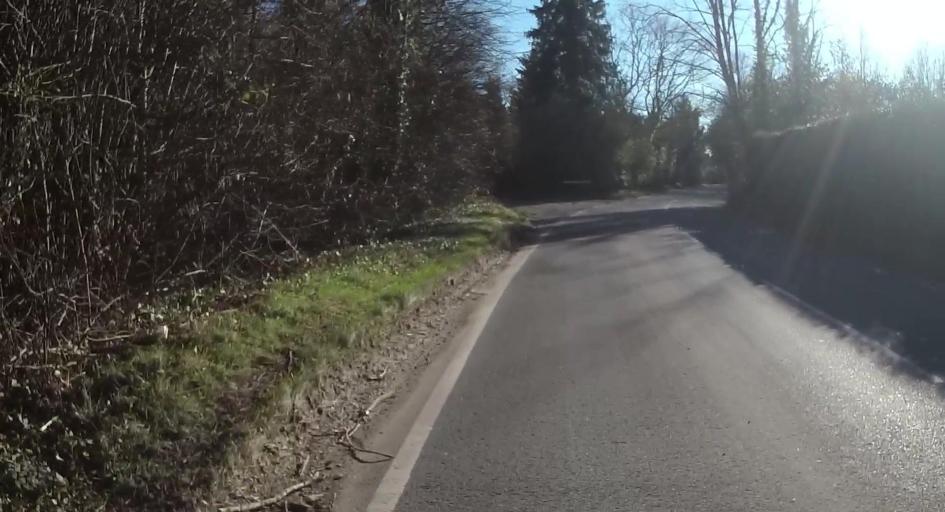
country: GB
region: England
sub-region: Surrey
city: Knaphill
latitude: 51.3243
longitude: -0.6176
